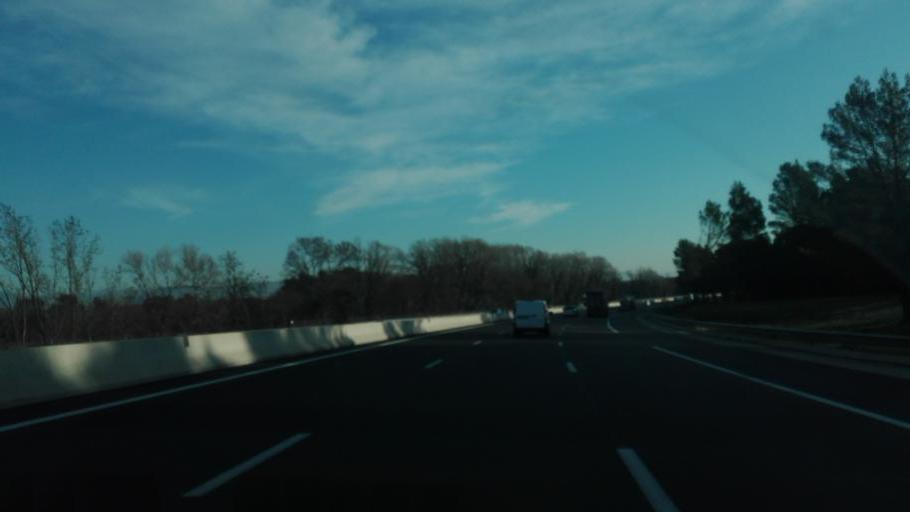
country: FR
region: Provence-Alpes-Cote d'Azur
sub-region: Departement du Var
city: La Motte
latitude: 43.4553
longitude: 6.5273
